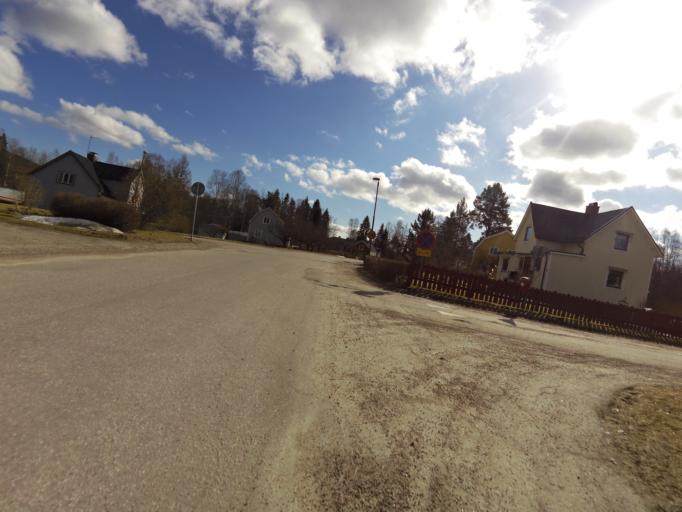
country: SE
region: Gaevleborg
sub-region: Hofors Kommun
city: Hofors
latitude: 60.5375
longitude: 16.2959
